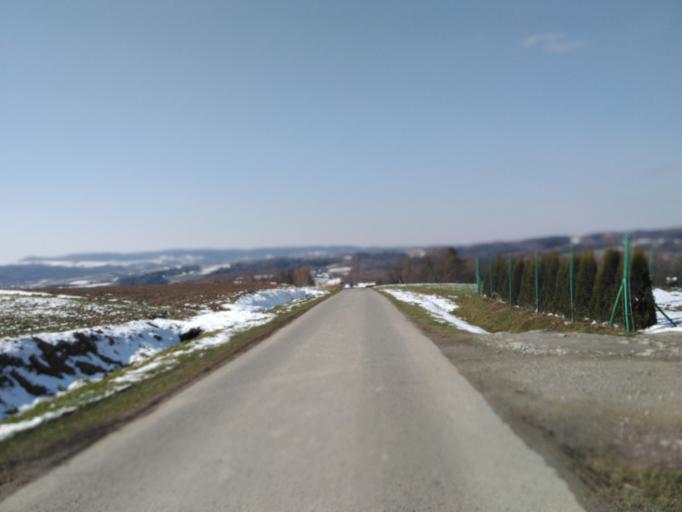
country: PL
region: Subcarpathian Voivodeship
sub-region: Powiat ropczycko-sedziszowski
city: Wielopole Skrzynskie
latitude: 49.9691
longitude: 21.5965
